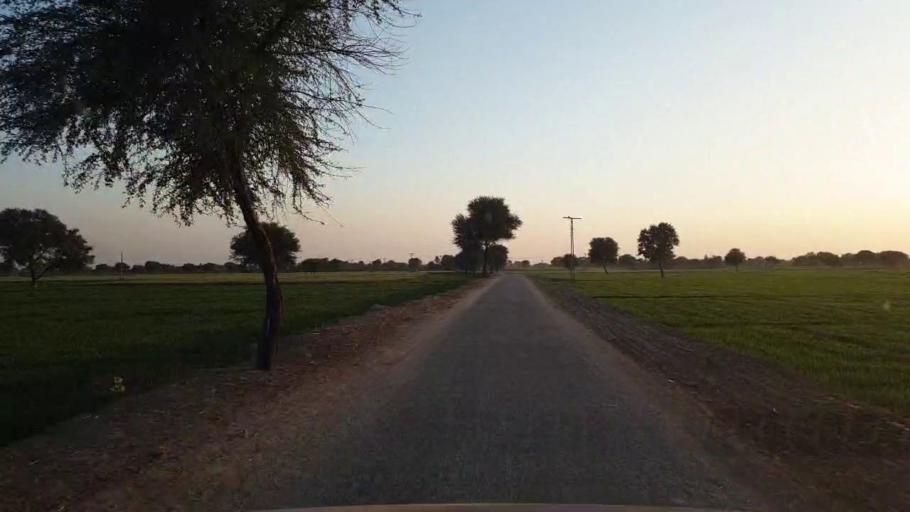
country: PK
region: Sindh
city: Tando Jam
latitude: 25.3081
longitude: 68.6390
